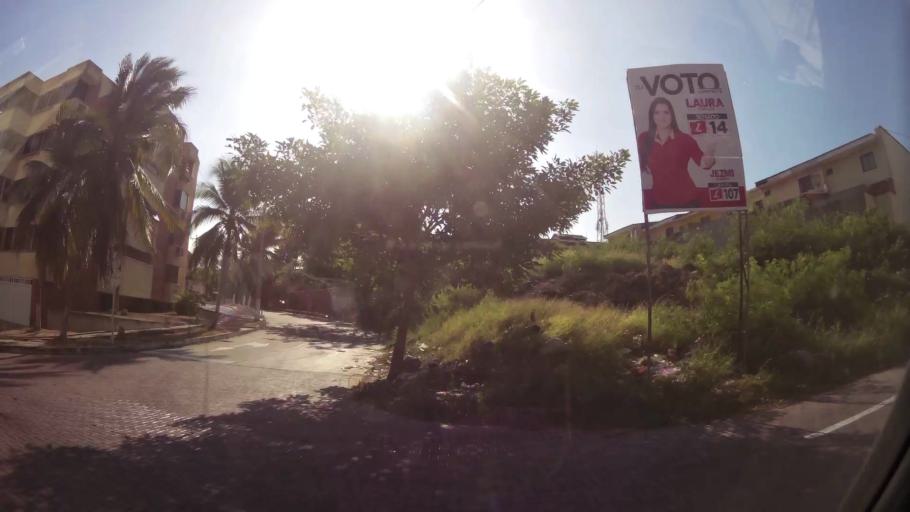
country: CO
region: Atlantico
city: Barranquilla
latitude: 11.0040
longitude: -74.8318
